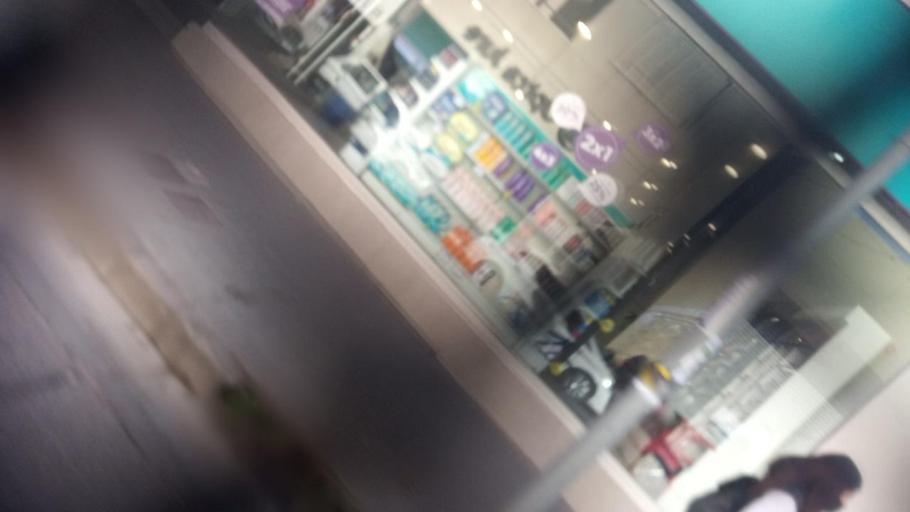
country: AR
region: Jujuy
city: San Salvador de Jujuy
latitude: -24.1841
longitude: -65.3041
